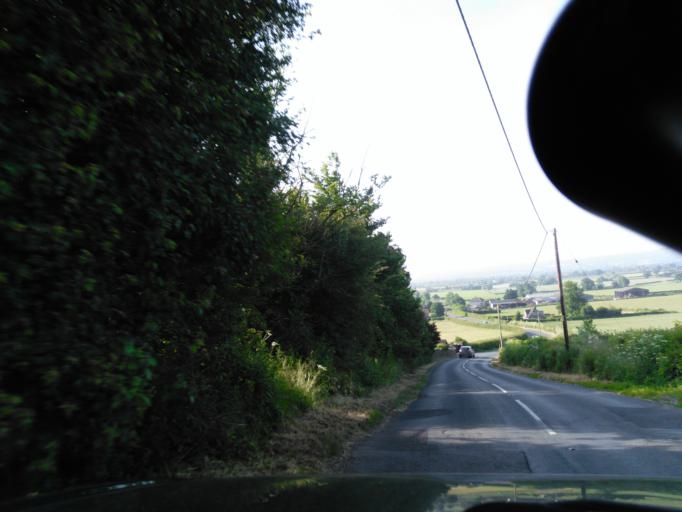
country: GB
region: England
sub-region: Wiltshire
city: Seend
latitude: 51.3464
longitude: -2.0872
